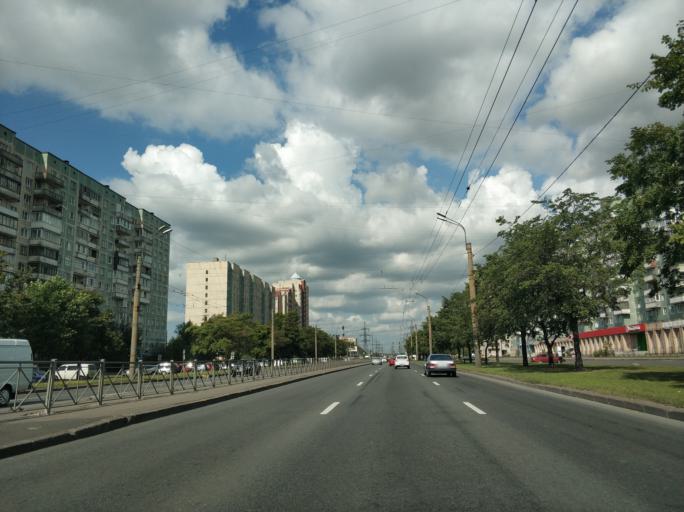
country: RU
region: St.-Petersburg
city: Krasnogvargeisky
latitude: 59.9525
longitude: 30.4706
